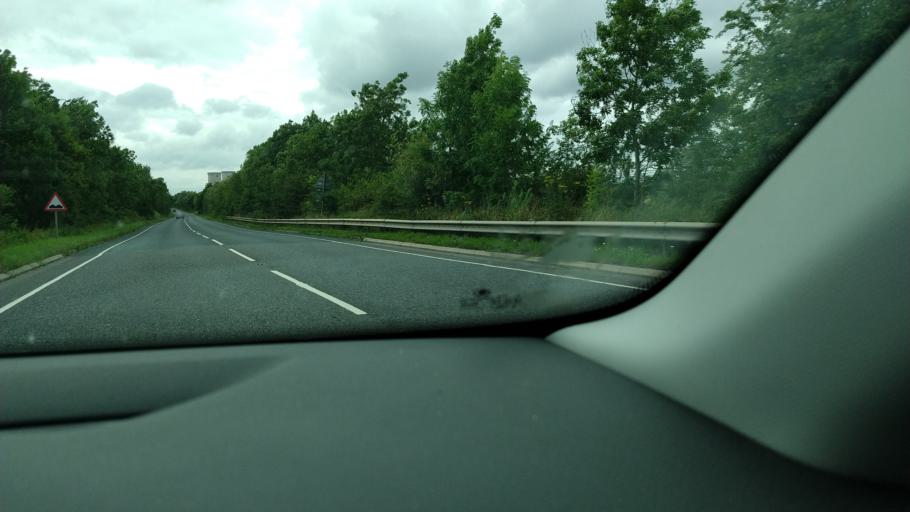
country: GB
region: England
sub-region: East Riding of Yorkshire
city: Rawcliffe
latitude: 53.7152
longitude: -0.9609
